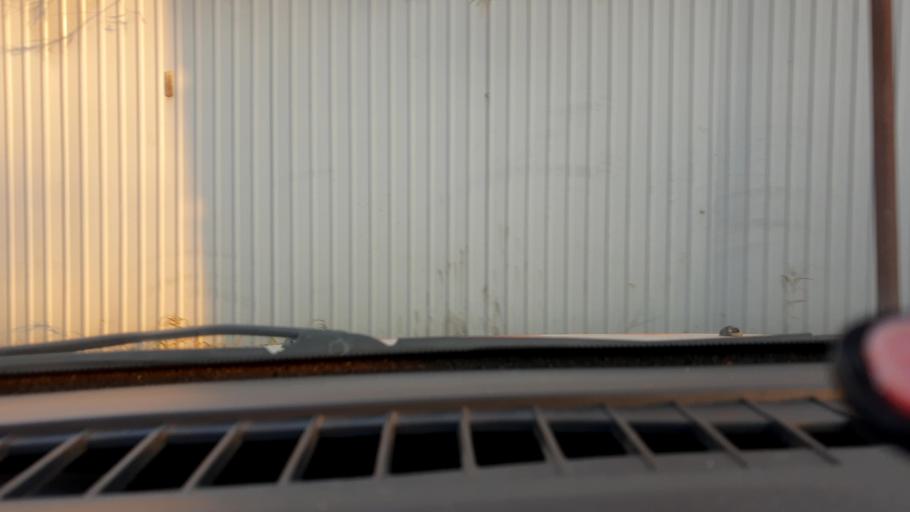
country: RU
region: Nizjnij Novgorod
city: Gorbatovka
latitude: 56.3083
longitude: 43.8240
